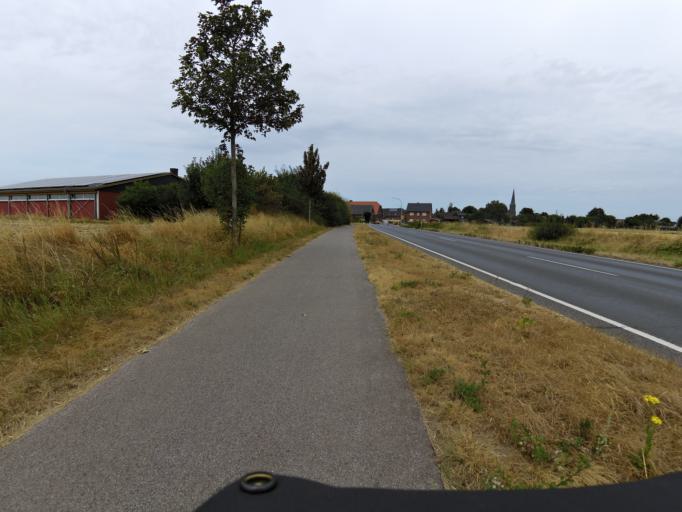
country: DE
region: North Rhine-Westphalia
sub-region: Regierungsbezirk Dusseldorf
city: Weeze
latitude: 51.5819
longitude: 6.1780
